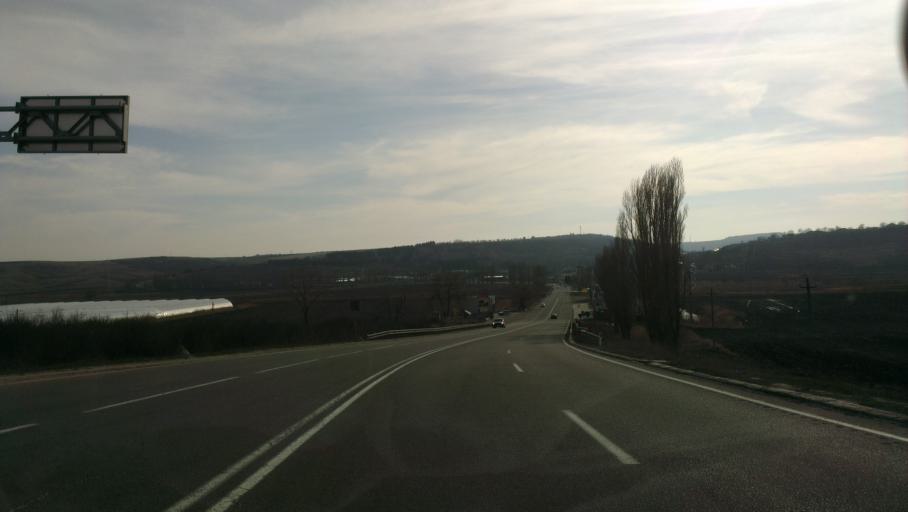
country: MD
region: Laloveni
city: Ialoveni
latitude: 46.9179
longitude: 28.6915
